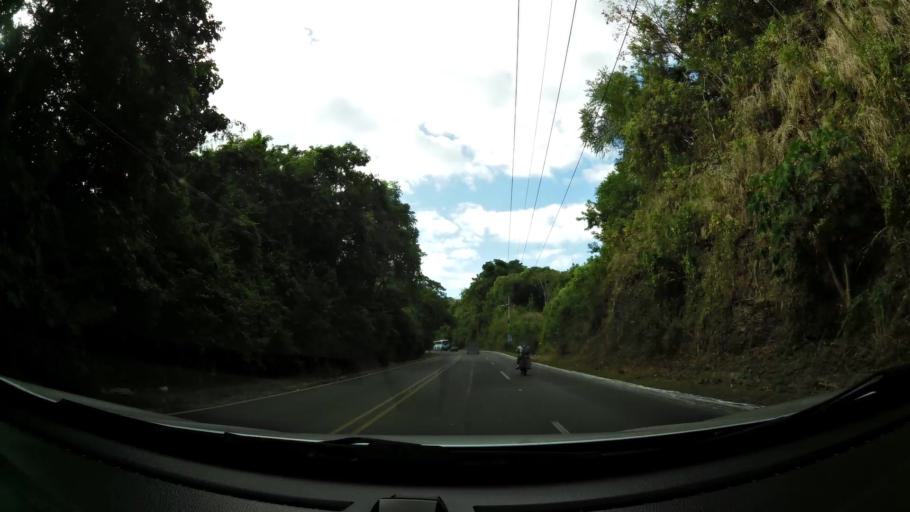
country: CR
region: Puntarenas
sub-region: Canton de Garabito
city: Jaco
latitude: 9.6804
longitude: -84.6476
